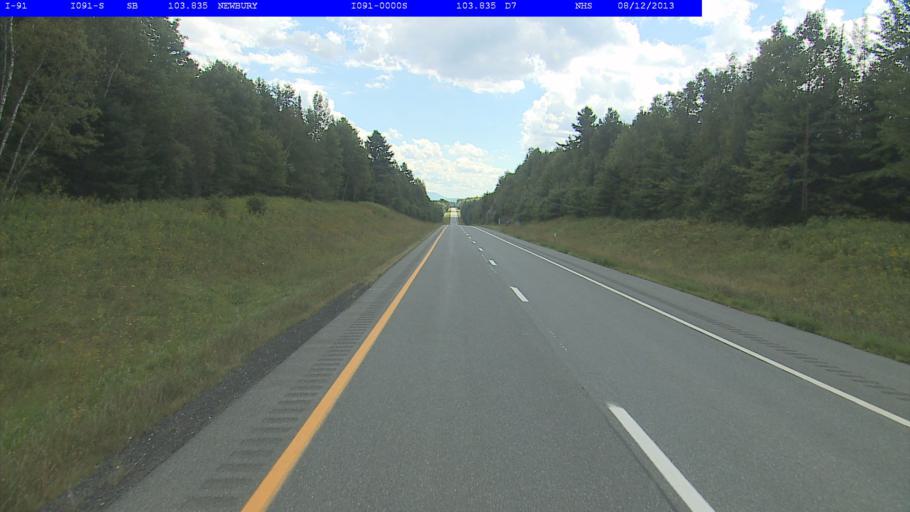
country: US
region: New Hampshire
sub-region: Grafton County
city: Haverhill
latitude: 44.0690
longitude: -72.1112
